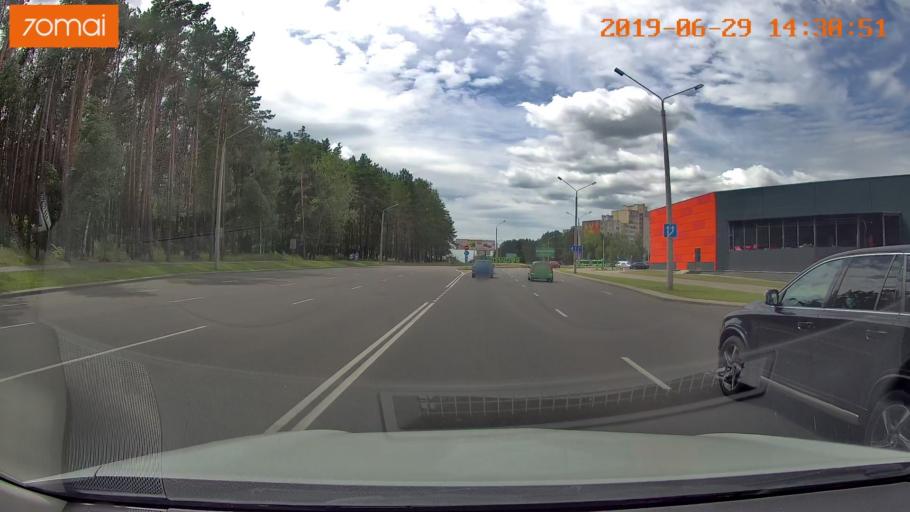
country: BY
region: Minsk
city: Salihorsk
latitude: 52.7814
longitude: 27.5131
